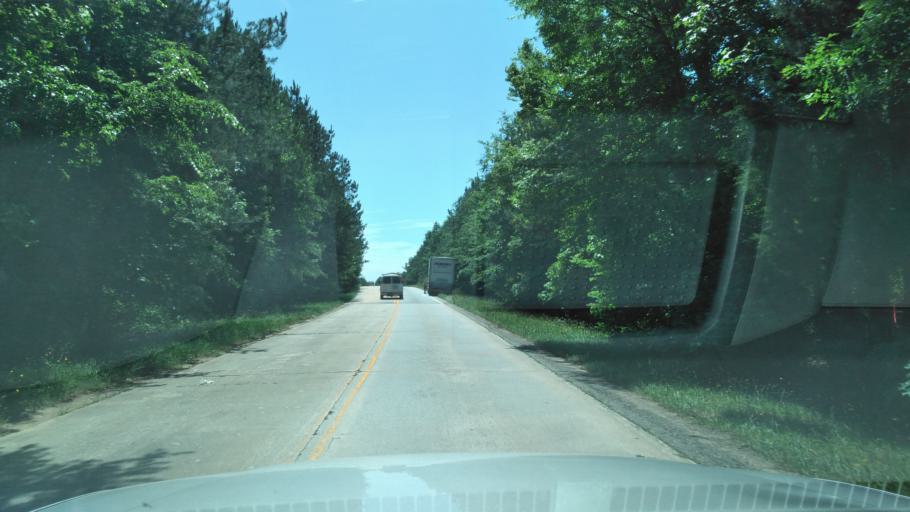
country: US
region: South Carolina
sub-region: Greenville County
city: Fountain Inn
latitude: 34.6419
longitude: -82.1490
